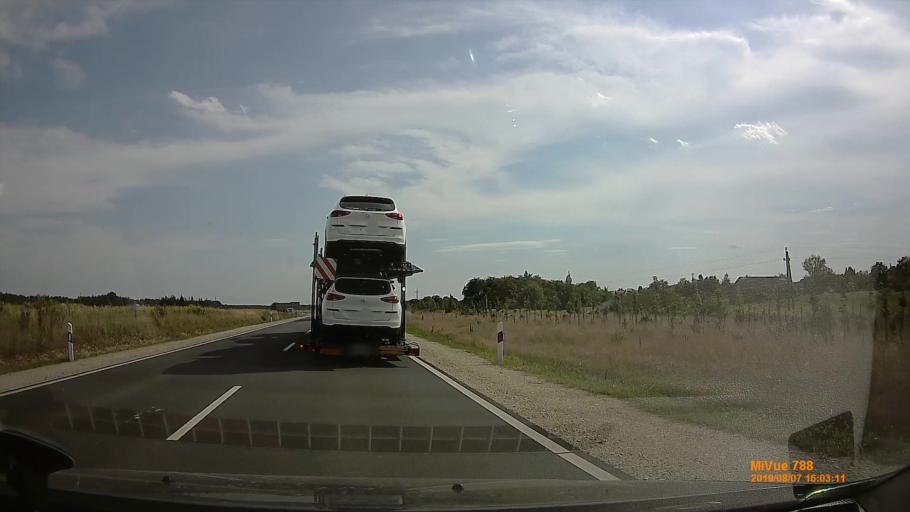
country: HU
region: Vas
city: Kormend
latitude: 46.9676
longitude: 16.6229
